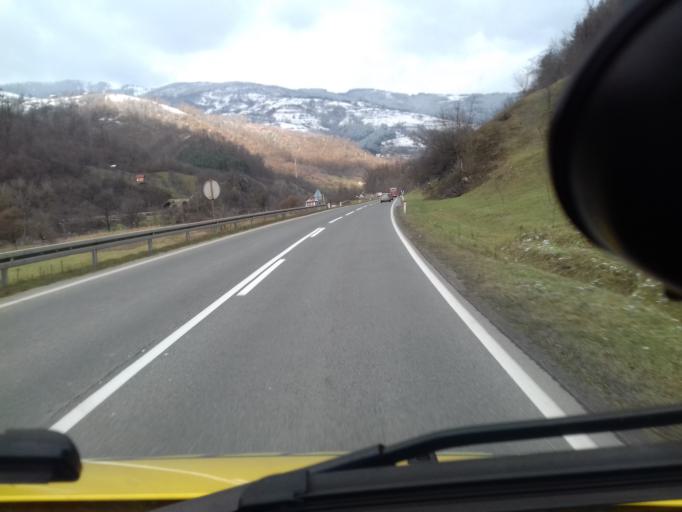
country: BA
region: Federation of Bosnia and Herzegovina
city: Zeljezno Polje
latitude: 44.3404
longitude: 17.9226
